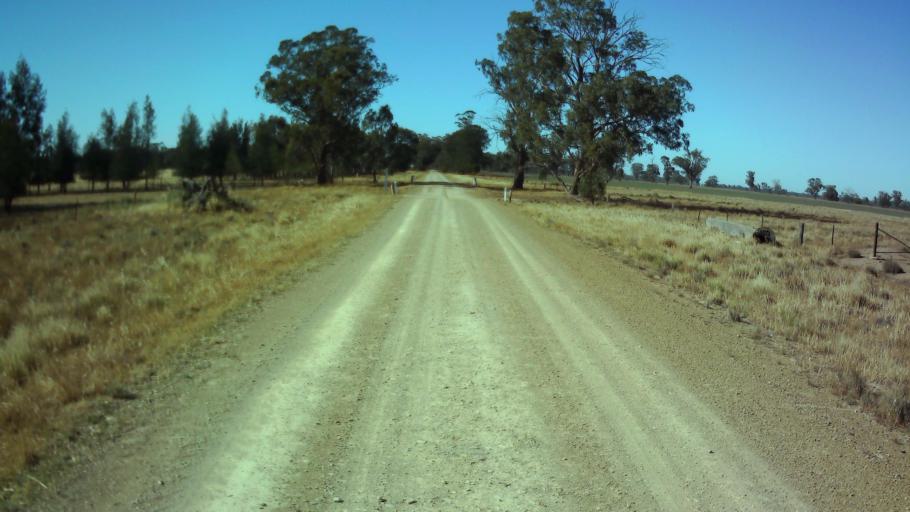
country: AU
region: New South Wales
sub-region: Weddin
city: Grenfell
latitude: -33.9319
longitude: 147.8727
